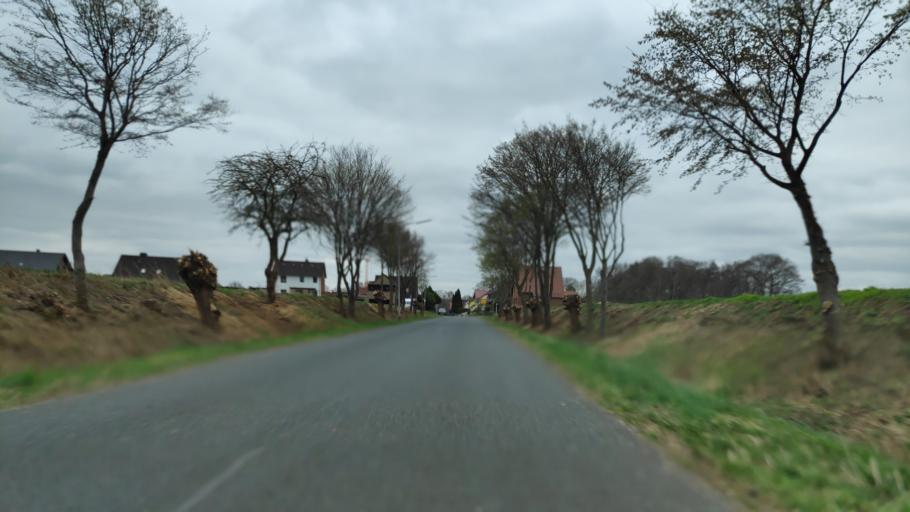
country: DE
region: North Rhine-Westphalia
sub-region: Regierungsbezirk Detmold
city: Petershagen
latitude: 52.3483
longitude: 8.9305
